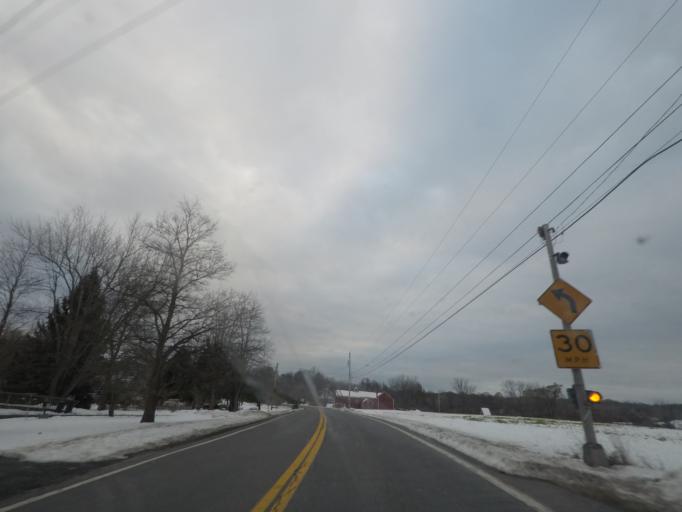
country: US
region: New York
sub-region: Ulster County
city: Clintondale
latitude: 41.6887
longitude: -74.1050
